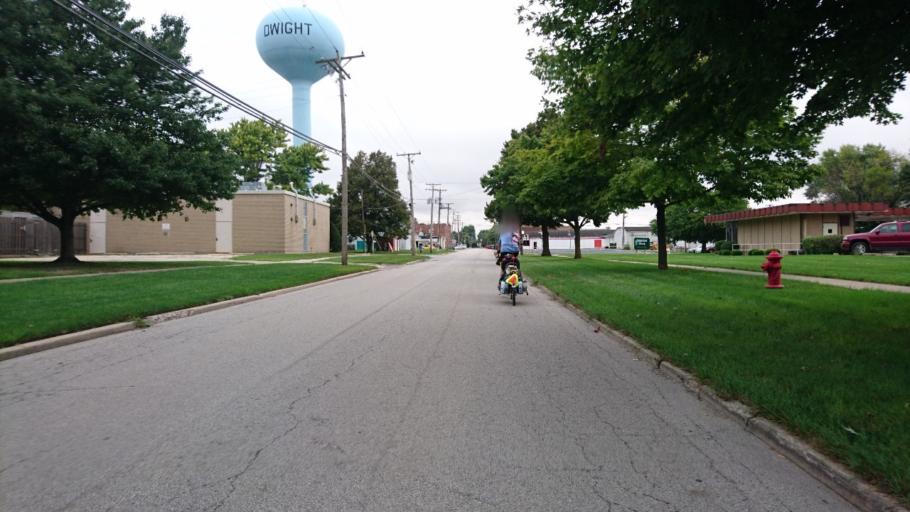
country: US
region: Illinois
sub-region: Livingston County
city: Dwight
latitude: 41.0913
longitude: -88.4259
